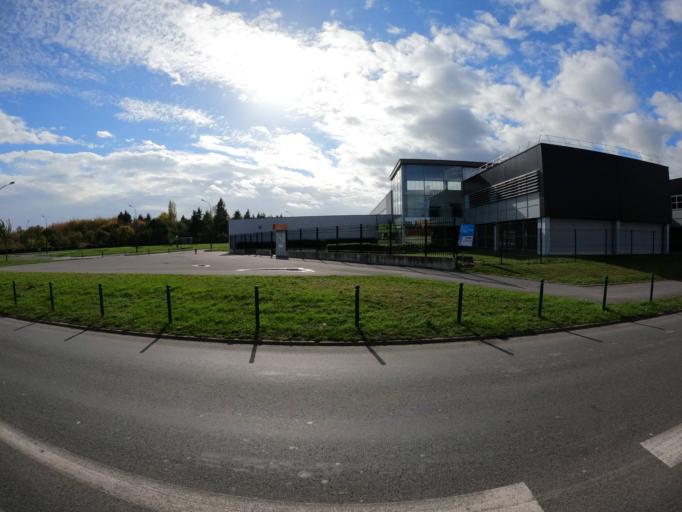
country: FR
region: Ile-de-France
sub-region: Departement de Seine-et-Marne
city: Saint-Germain-sur-Morin
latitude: 48.8838
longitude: 2.8440
